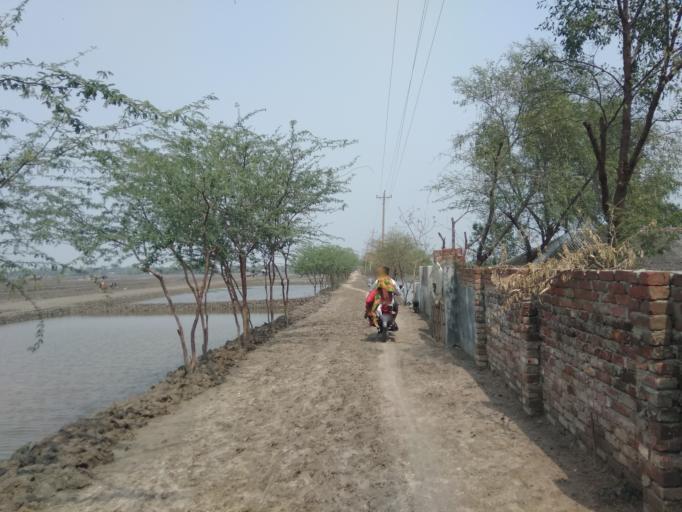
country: IN
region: West Bengal
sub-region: North 24 Parganas
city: Taki
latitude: 22.2759
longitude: 89.2843
